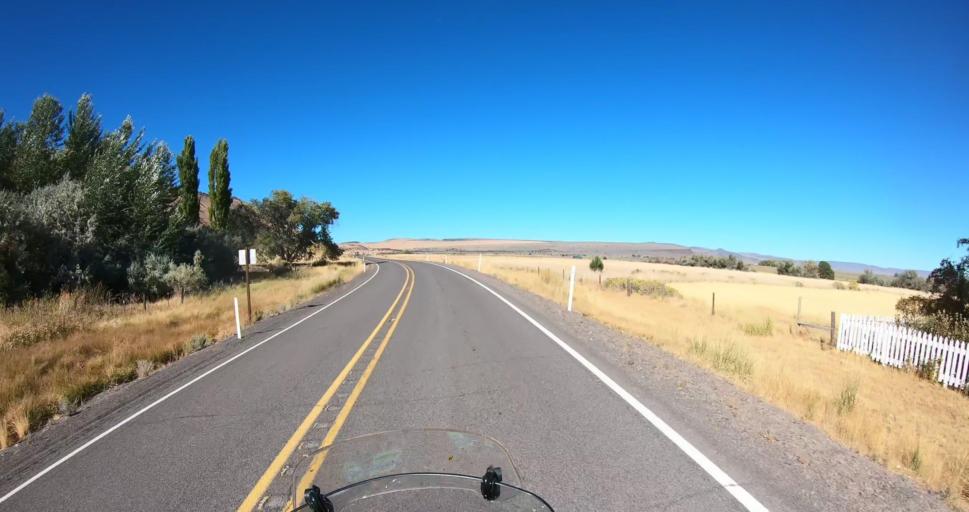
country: US
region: Oregon
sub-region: Lake County
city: Lakeview
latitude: 42.9735
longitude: -120.7778
